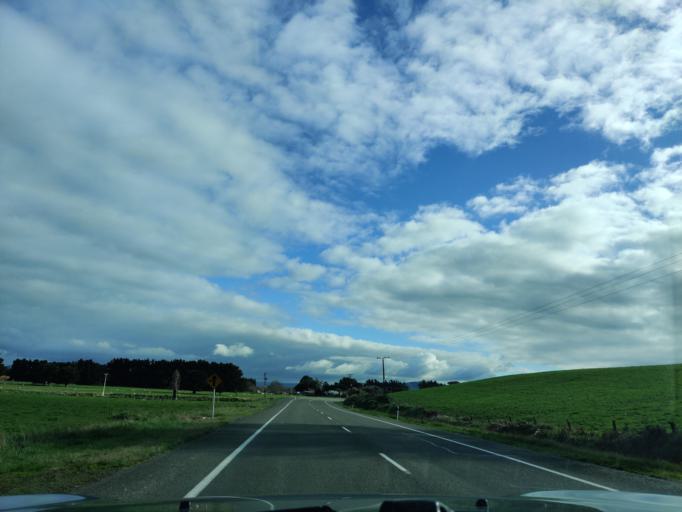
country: NZ
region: Manawatu-Wanganui
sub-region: Palmerston North City
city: Palmerston North
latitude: -40.3399
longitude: 175.8880
